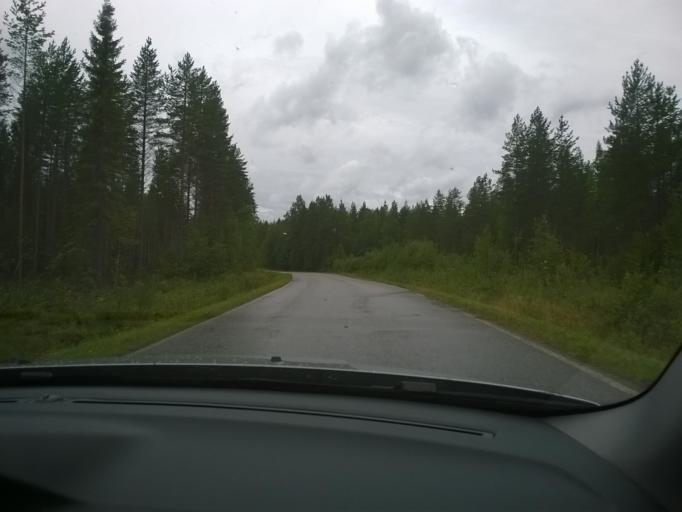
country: FI
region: Kainuu
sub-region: Kehys-Kainuu
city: Kuhmo
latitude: 64.1372
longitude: 29.4124
